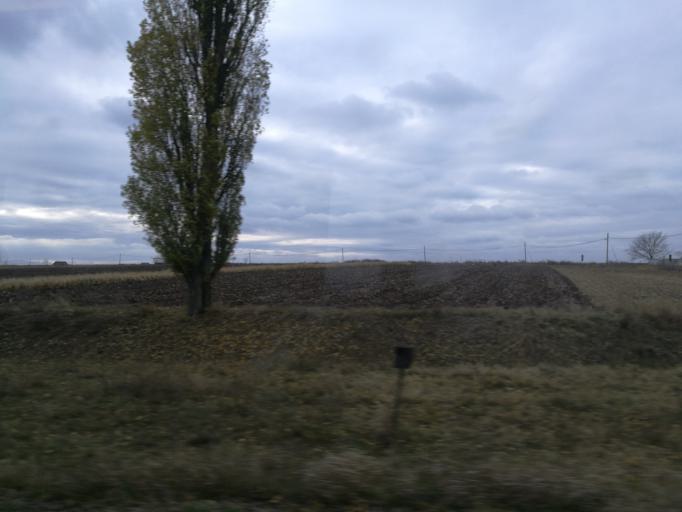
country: RO
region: Iasi
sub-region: Comuna Mircesti
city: Iugani
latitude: 47.0558
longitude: 26.8477
